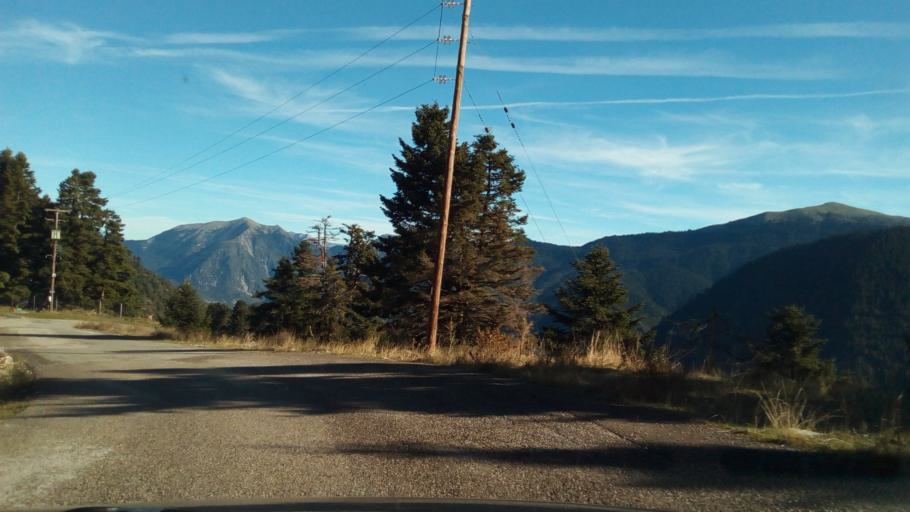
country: GR
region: West Greece
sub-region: Nomos Aitolias kai Akarnanias
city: Nafpaktos
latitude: 38.5355
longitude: 21.8407
